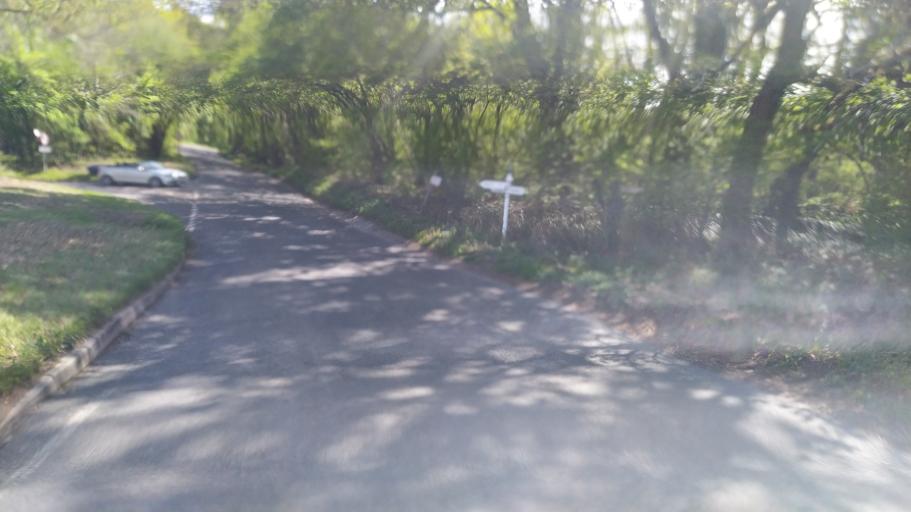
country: GB
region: England
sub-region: Dorset
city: Alderholt
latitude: 50.8946
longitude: -1.8107
